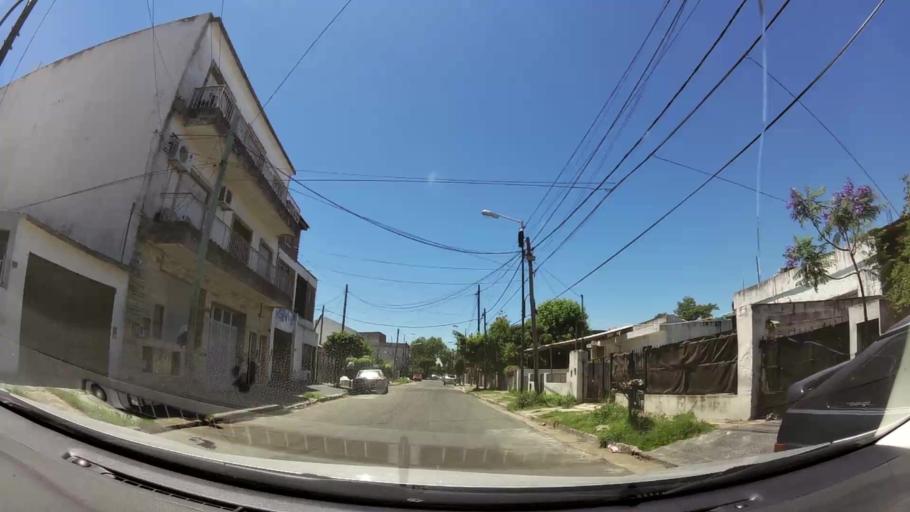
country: AR
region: Buenos Aires
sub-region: Partido de Tigre
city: Tigre
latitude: -34.4528
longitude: -58.5586
